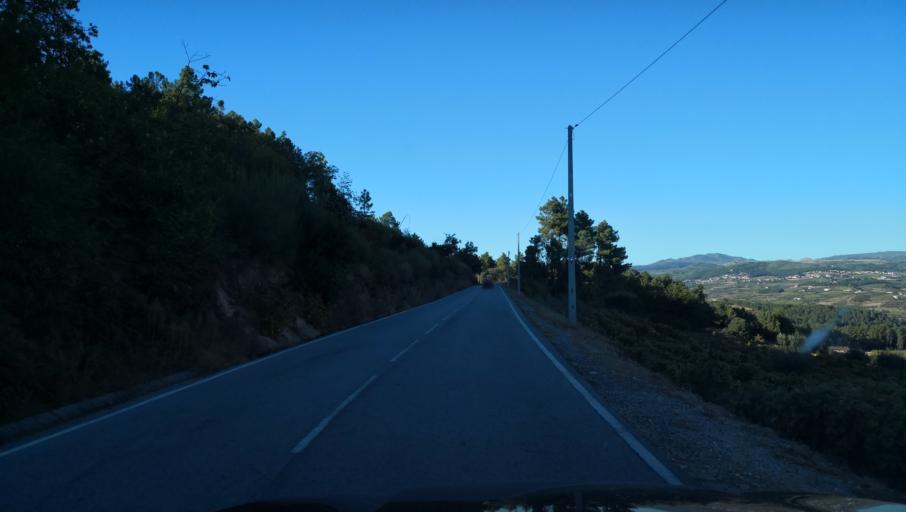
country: PT
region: Vila Real
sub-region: Sabrosa
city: Sabrosa
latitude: 41.2779
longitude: -7.5688
